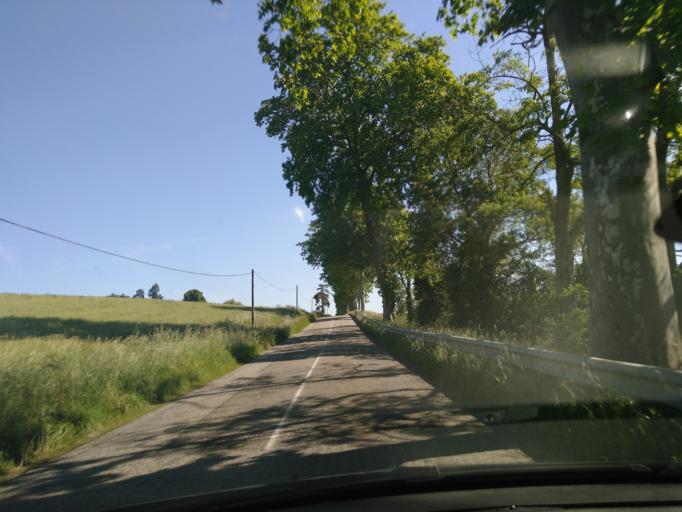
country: FR
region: Midi-Pyrenees
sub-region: Departement du Gers
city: Gimont
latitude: 43.5914
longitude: 0.8358
